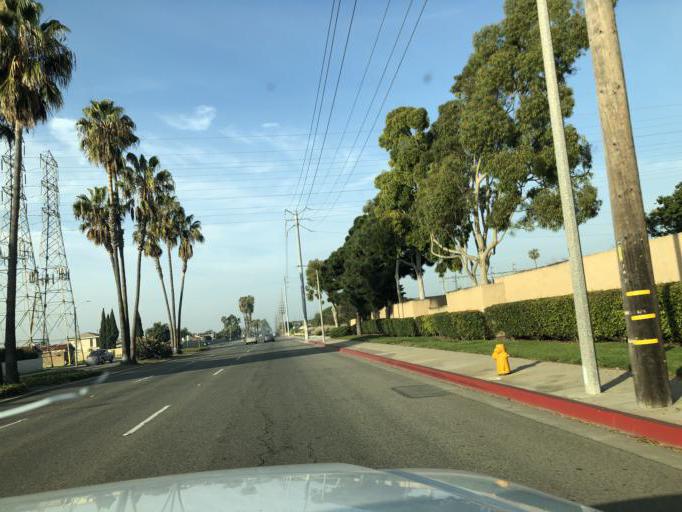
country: US
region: California
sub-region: Orange County
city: Costa Mesa
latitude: 33.6531
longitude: -117.9535
